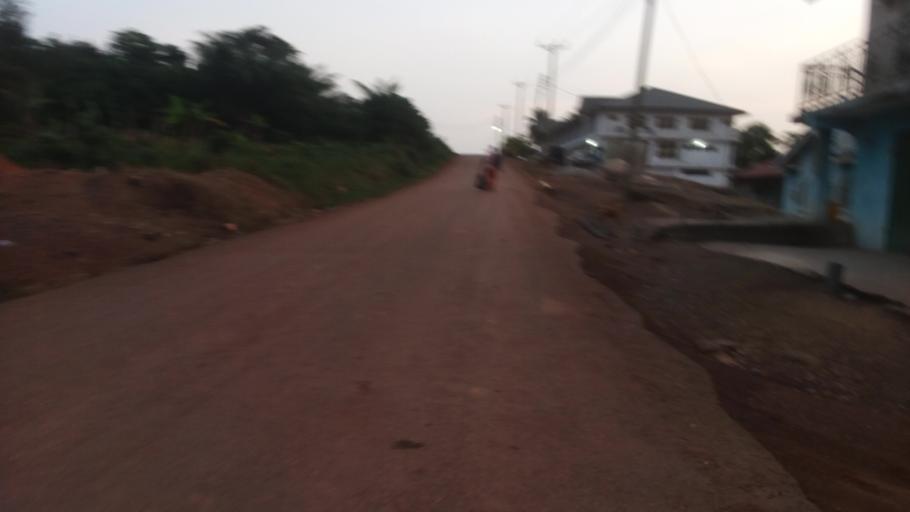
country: GH
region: Western
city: Tarkwa
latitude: 5.3069
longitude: -2.0009
